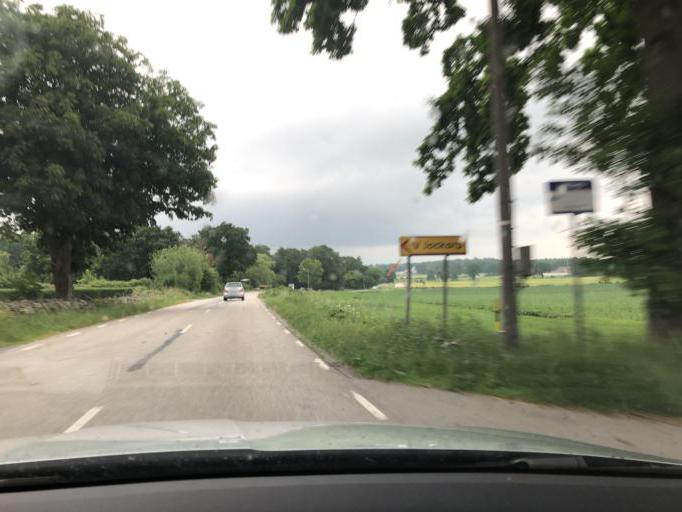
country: SE
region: Blekinge
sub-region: Solvesborgs Kommun
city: Soelvesborg
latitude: 56.0871
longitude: 14.6063
